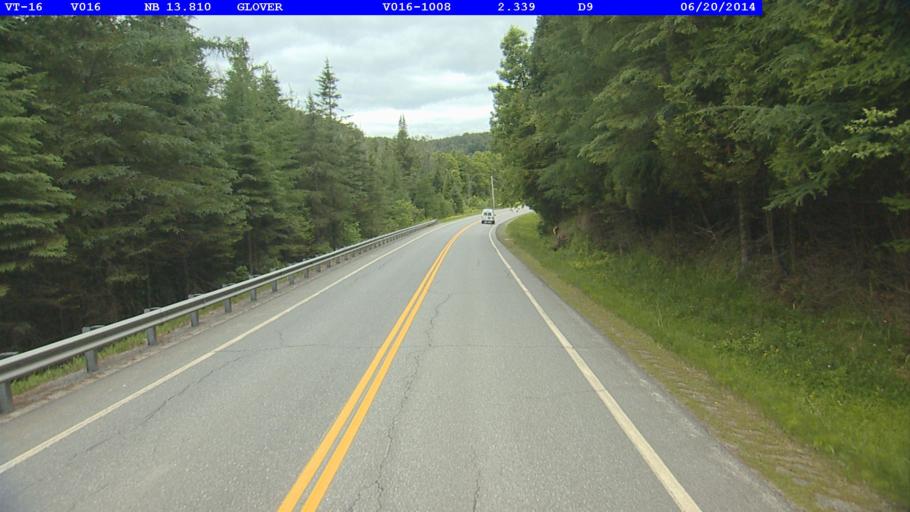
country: US
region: Vermont
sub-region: Caledonia County
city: Hardwick
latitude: 44.6577
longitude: -72.1980
